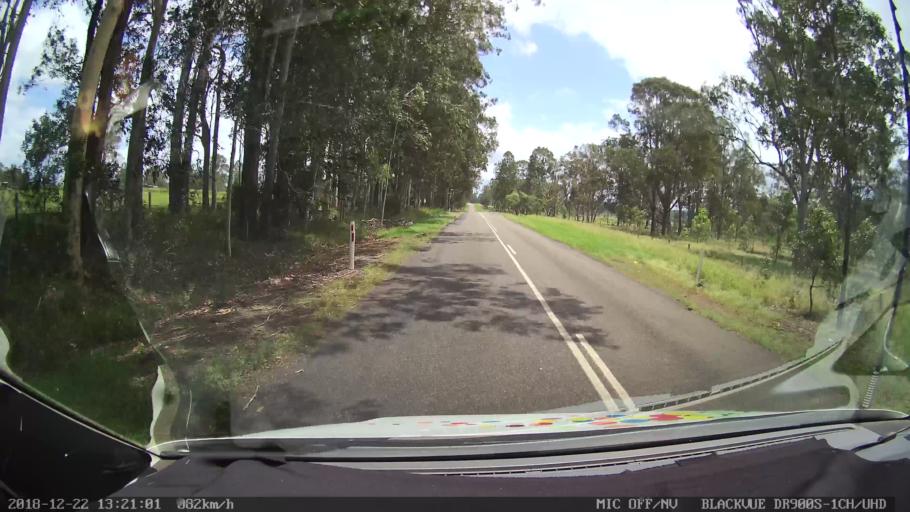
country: AU
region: New South Wales
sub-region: Clarence Valley
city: Coutts Crossing
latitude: -29.7727
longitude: 152.9241
